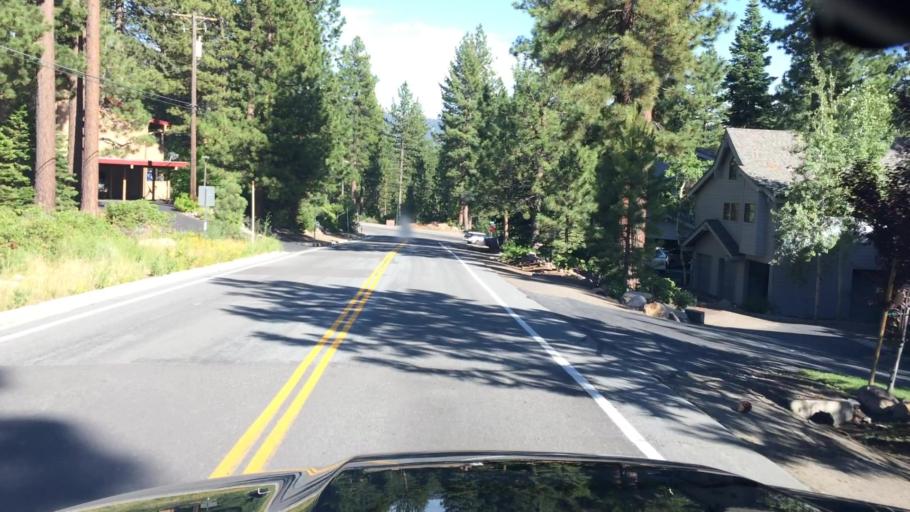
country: US
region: Nevada
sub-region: Washoe County
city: Incline Village
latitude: 39.2536
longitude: -119.9581
